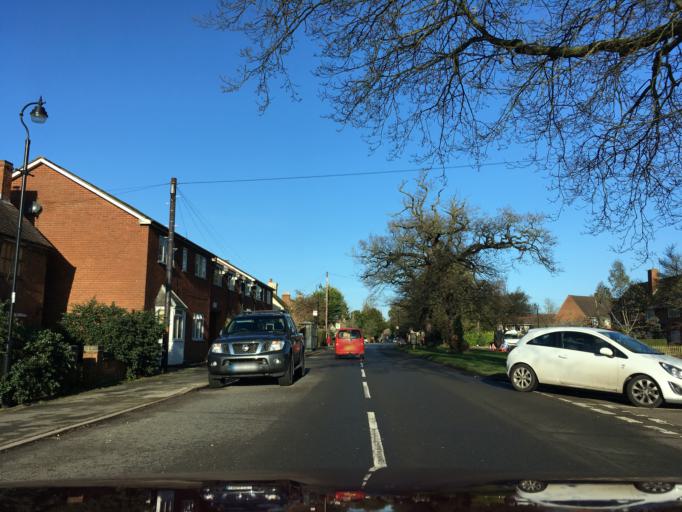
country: GB
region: England
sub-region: Warwickshire
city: Warwick
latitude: 52.2398
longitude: -1.6061
